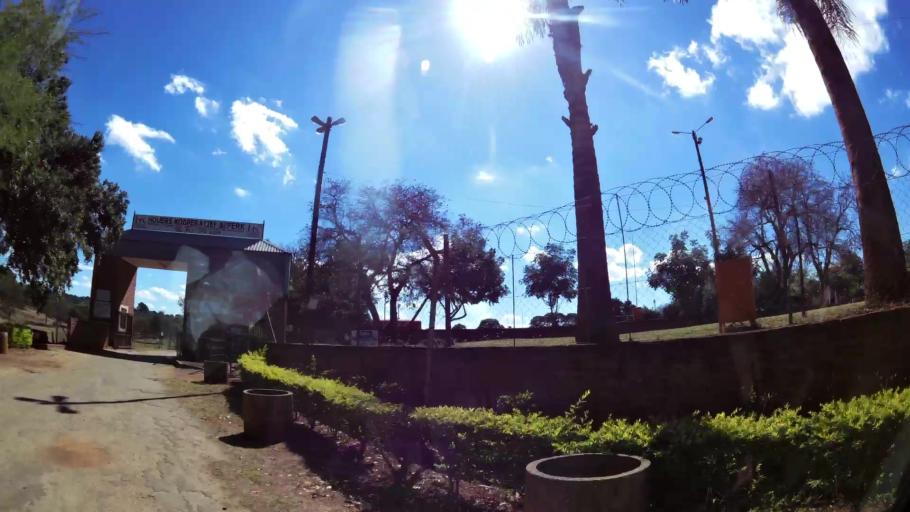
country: ZA
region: Limpopo
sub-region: Mopani District Municipality
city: Tzaneen
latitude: -23.8199
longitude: 30.1637
